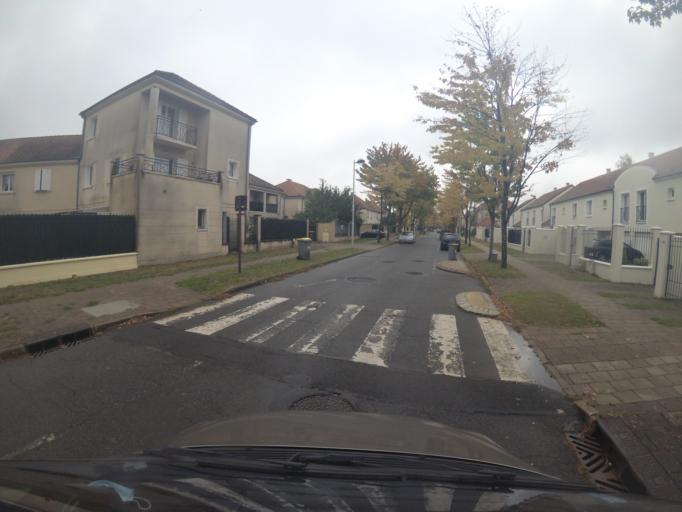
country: FR
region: Ile-de-France
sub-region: Departement de Seine-et-Marne
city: Bussy-Saint-Georges
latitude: 48.8411
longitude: 2.7154
